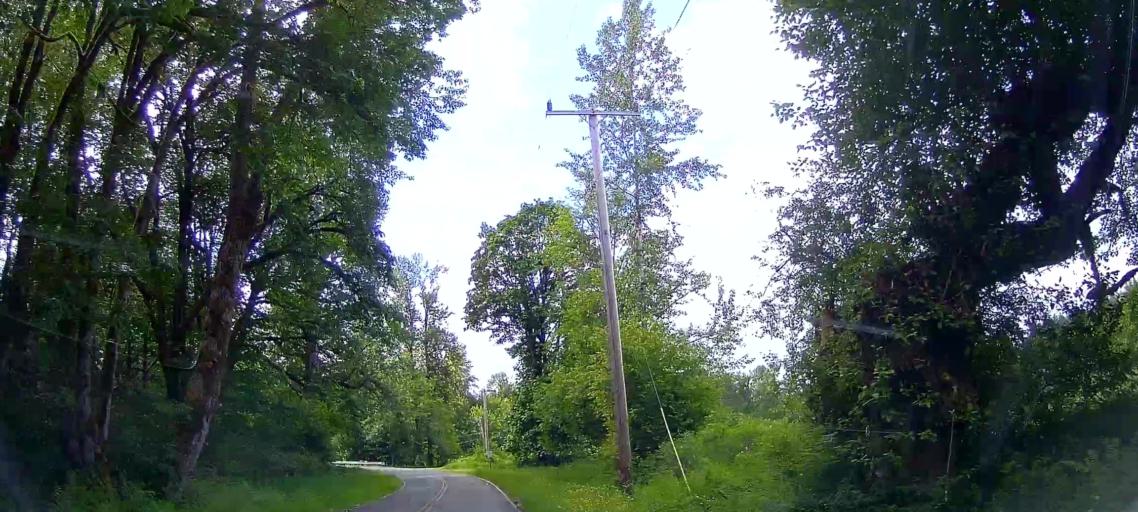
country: US
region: Washington
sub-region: Skagit County
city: Sedro-Woolley
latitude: 48.6781
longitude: -122.1626
